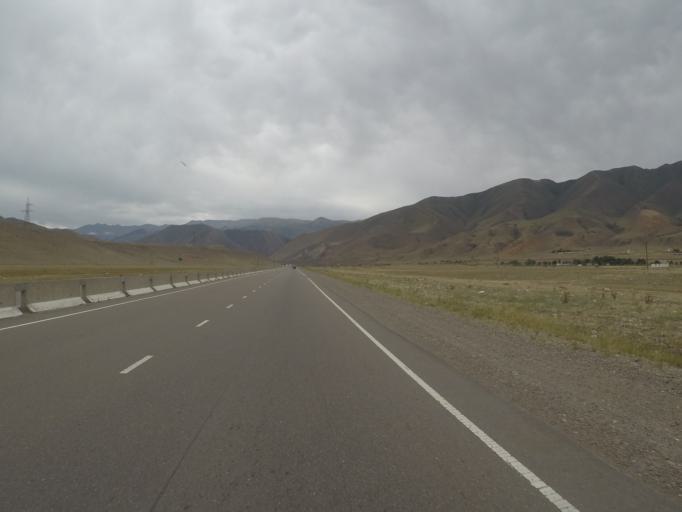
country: KG
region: Chuy
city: Bystrovka
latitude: 42.7161
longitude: 75.8507
